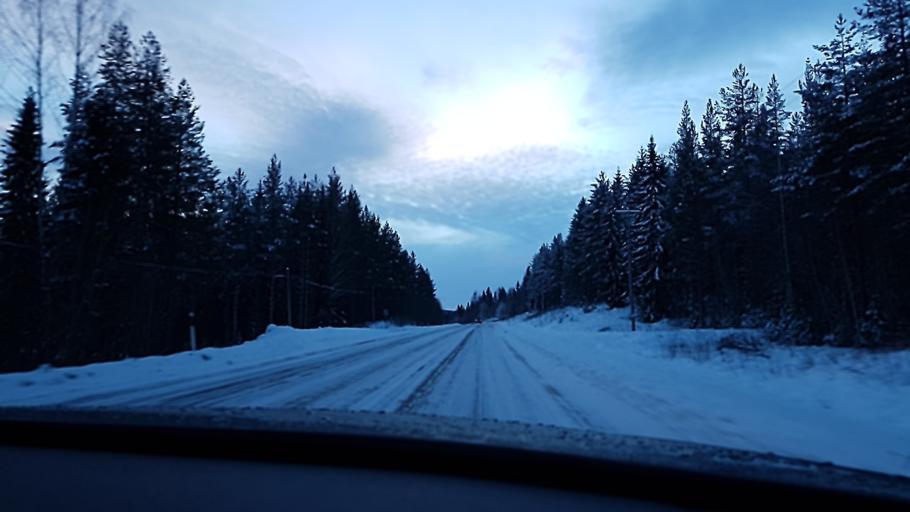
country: SE
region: Jaemtland
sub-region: Harjedalens Kommun
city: Sveg
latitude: 62.0802
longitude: 14.9461
